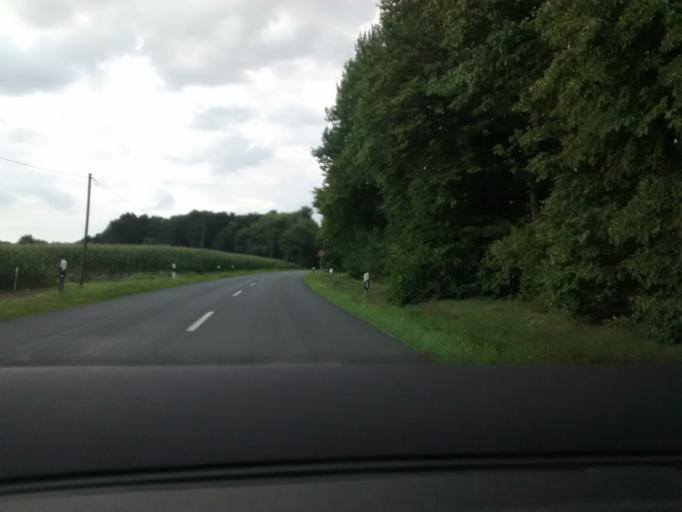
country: DE
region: Lower Saxony
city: Scharnebeck
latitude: 53.3098
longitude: 10.5011
